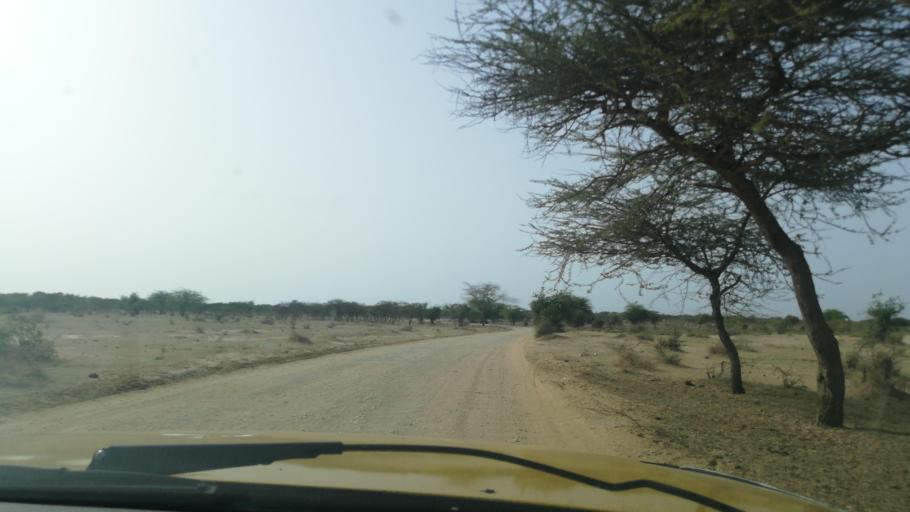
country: SN
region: Saint-Louis
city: Saint-Louis
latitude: 16.0583
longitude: -16.3326
